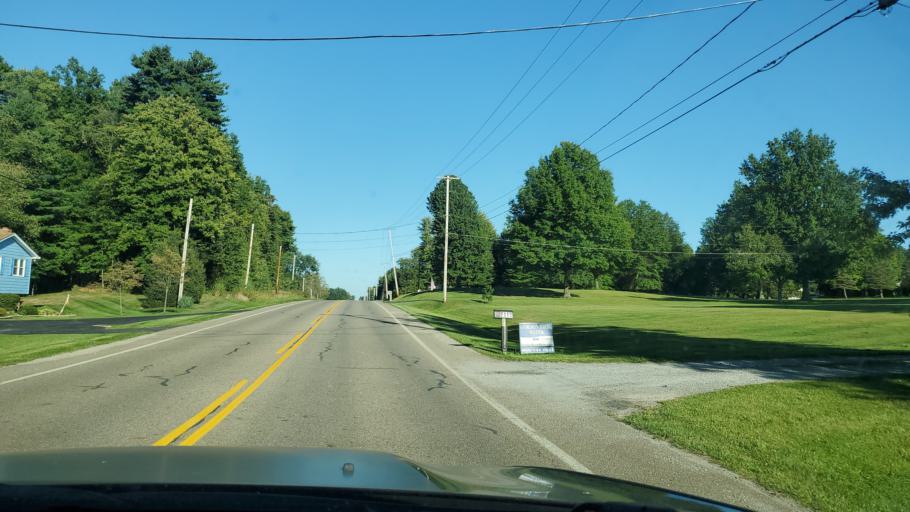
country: US
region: Ohio
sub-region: Mahoning County
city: Canfield
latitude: 40.9883
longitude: -80.7857
